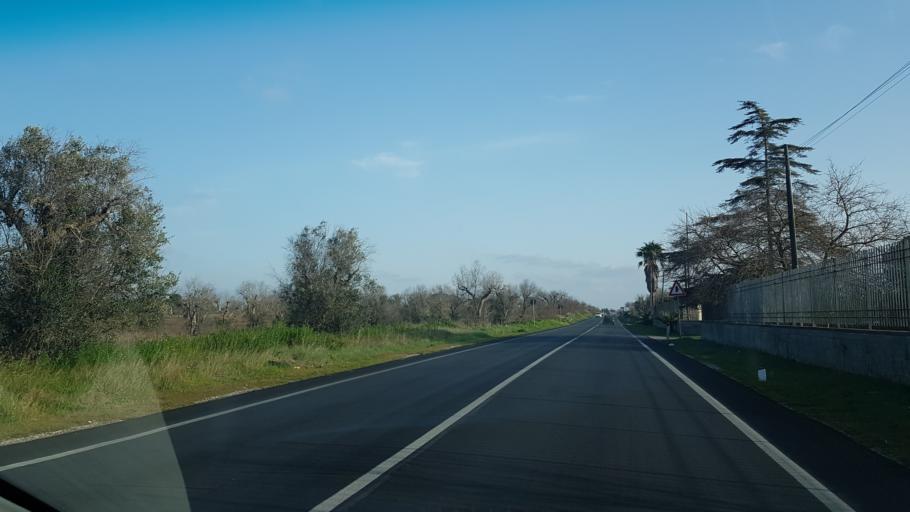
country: IT
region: Apulia
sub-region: Provincia di Lecce
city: Trepuzzi
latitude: 40.4177
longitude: 18.0610
